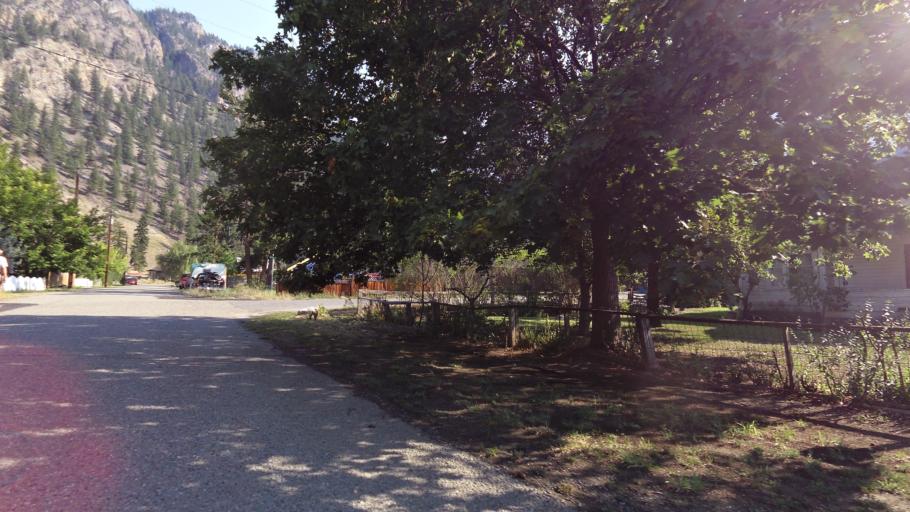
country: CA
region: British Columbia
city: Princeton
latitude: 49.3578
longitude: -120.0777
